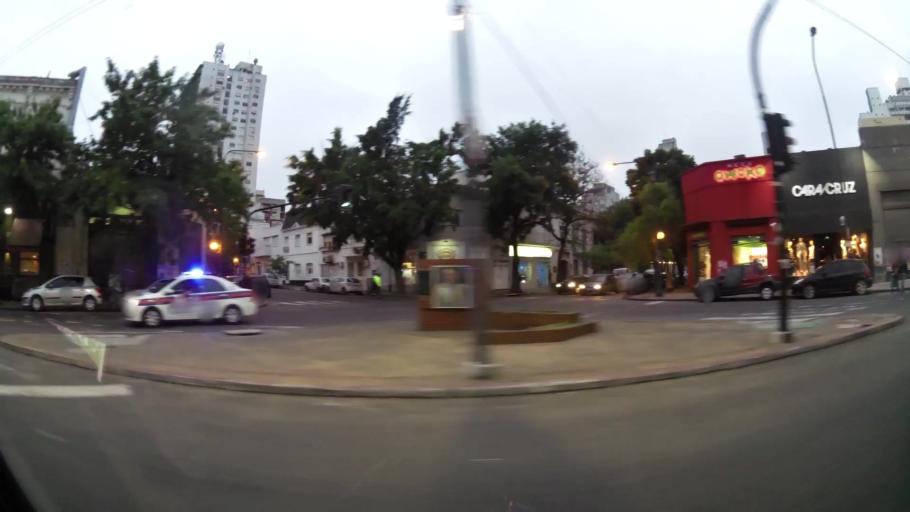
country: AR
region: Buenos Aires
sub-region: Partido de La Plata
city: La Plata
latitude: -34.9180
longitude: -57.9548
